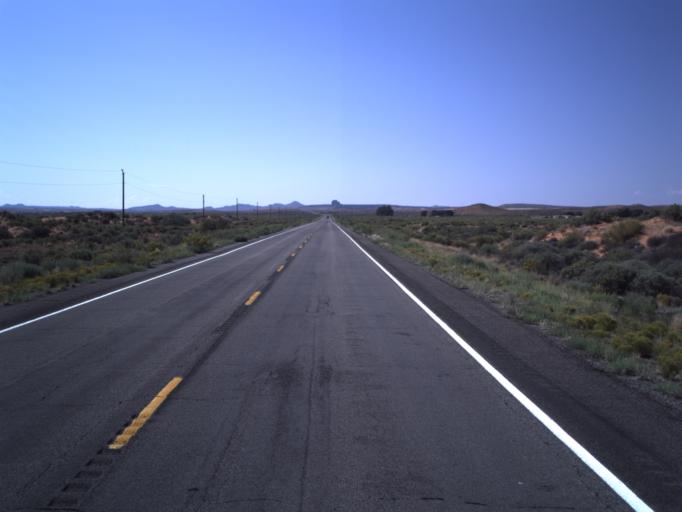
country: US
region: Utah
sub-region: San Juan County
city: Blanding
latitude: 37.1163
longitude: -109.5453
